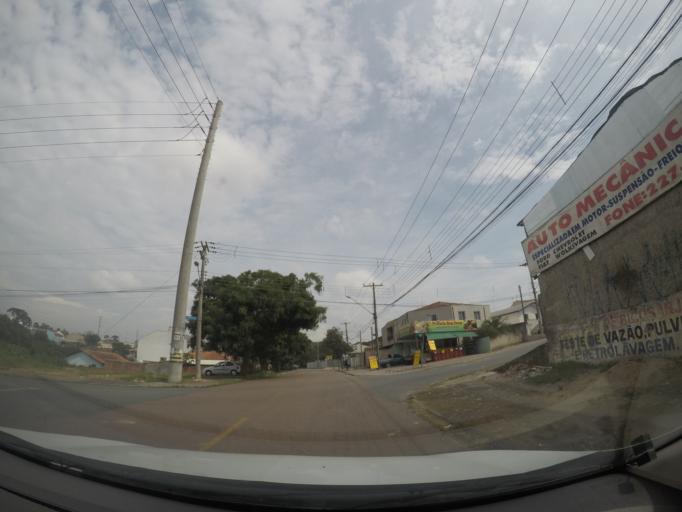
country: BR
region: Parana
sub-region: Sao Jose Dos Pinhais
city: Sao Jose dos Pinhais
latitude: -25.5224
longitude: -49.2841
